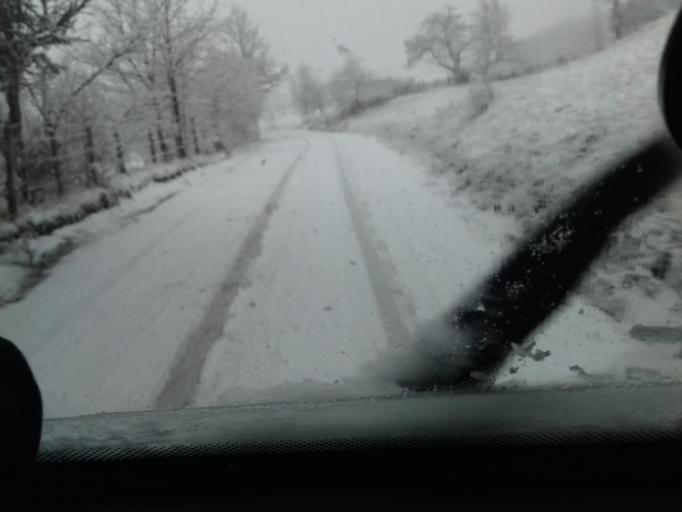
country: BA
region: Federation of Bosnia and Herzegovina
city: Lokvine
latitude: 44.2420
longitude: 17.8102
